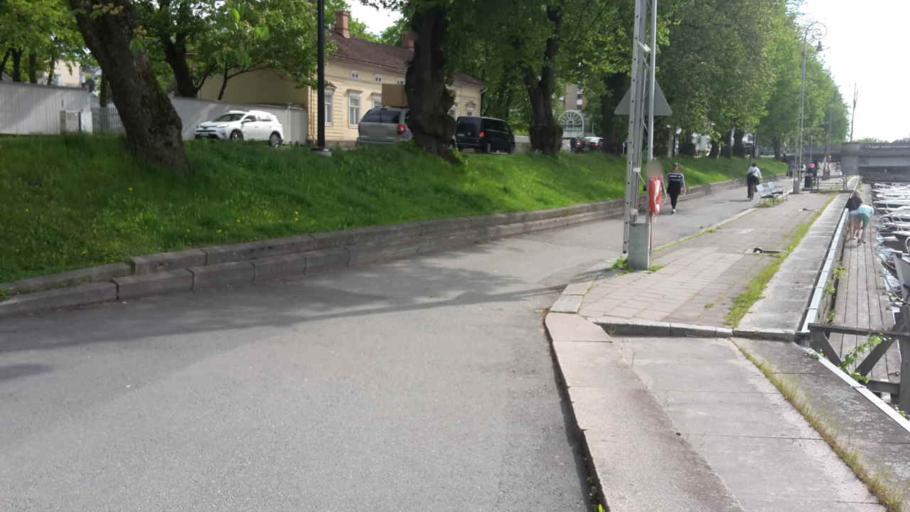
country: FI
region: Varsinais-Suomi
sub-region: Turku
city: Turku
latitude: 60.4447
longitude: 22.2579
